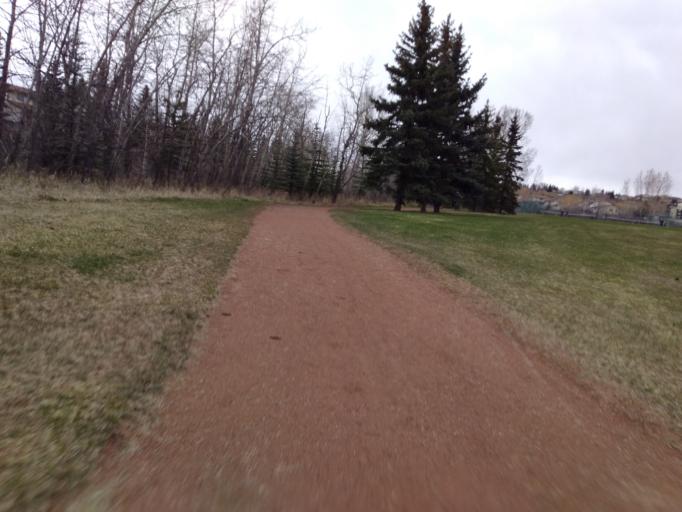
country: CA
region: Alberta
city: Cochrane
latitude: 51.1869
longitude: -114.4809
